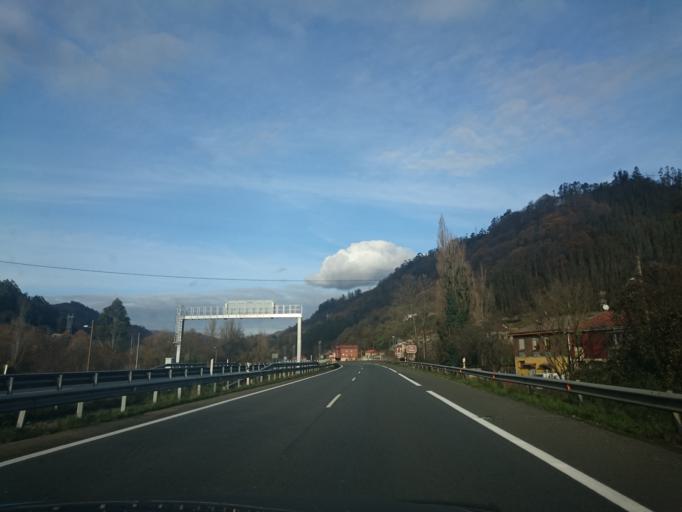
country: ES
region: Asturias
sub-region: Province of Asturias
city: Mieres
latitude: 43.2107
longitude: -5.7858
